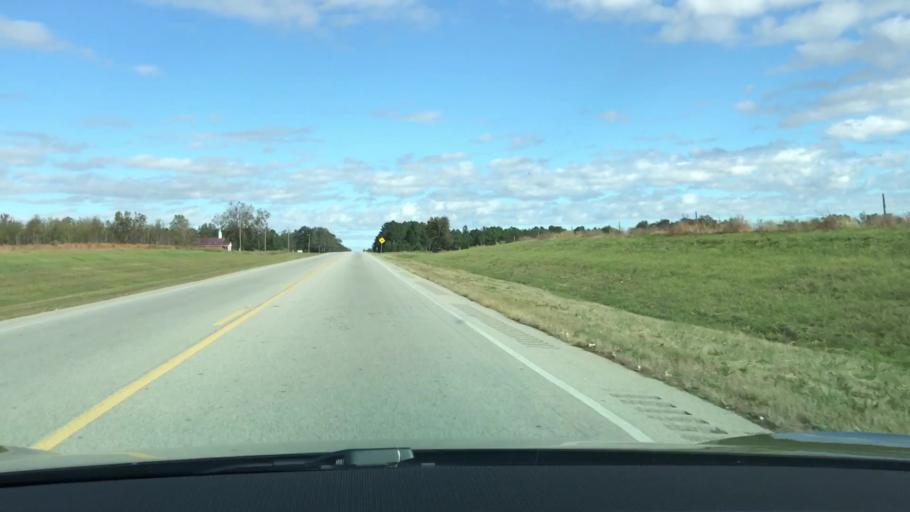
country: US
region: Georgia
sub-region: Jefferson County
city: Louisville
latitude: 32.9454
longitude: -82.3951
